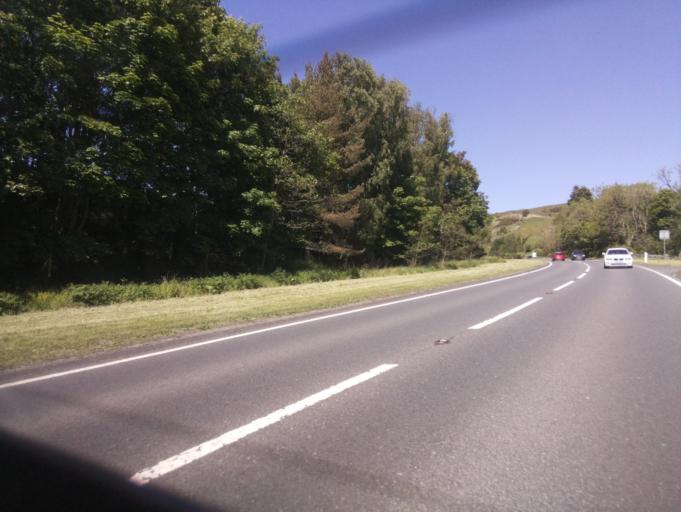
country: GB
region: Scotland
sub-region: The Scottish Borders
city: Selkirk
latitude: 55.4999
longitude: -2.8316
